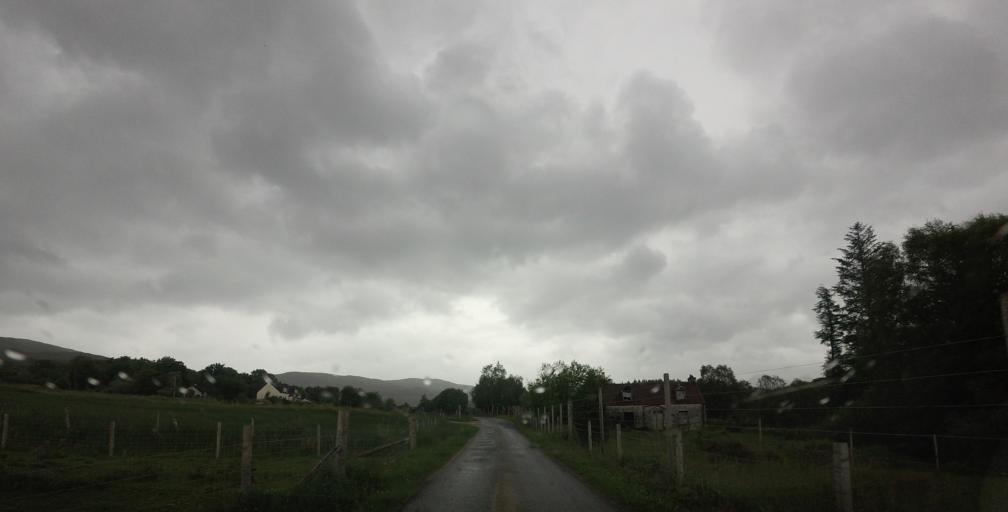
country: GB
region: Scotland
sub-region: Argyll and Bute
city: Oban
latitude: 56.7137
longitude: -5.5620
